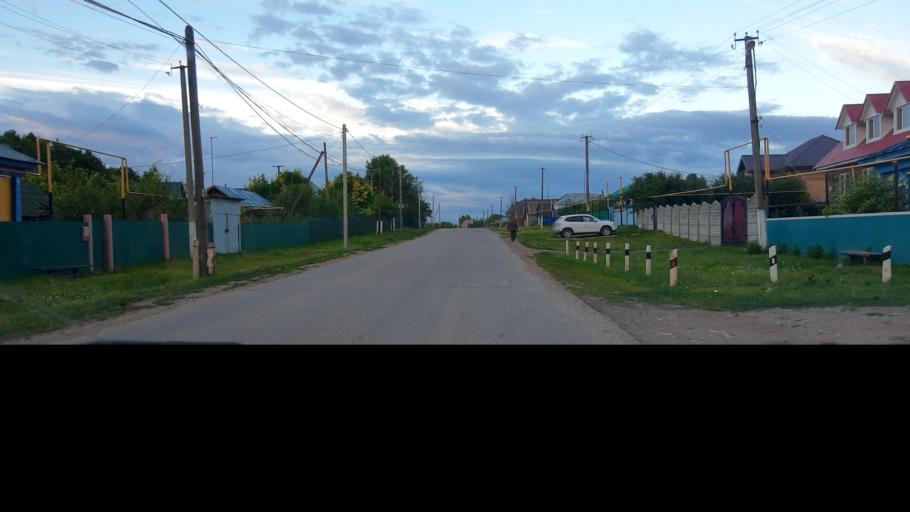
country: RU
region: Bashkortostan
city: Chishmy
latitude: 54.5573
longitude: 55.4663
